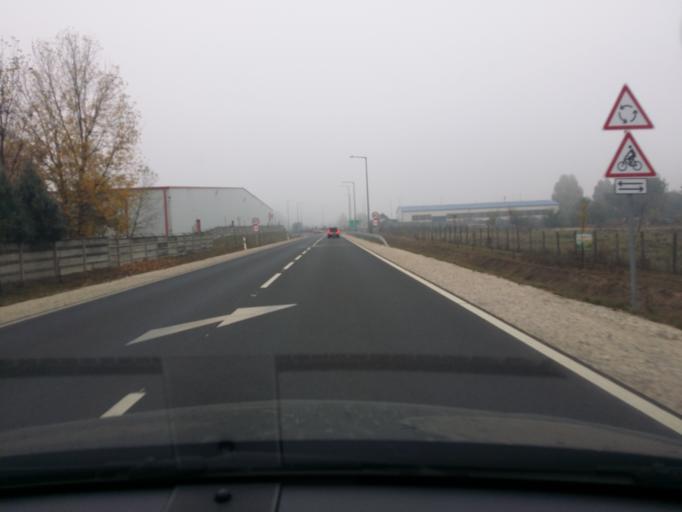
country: HU
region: Szabolcs-Szatmar-Bereg
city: Nyiregyhaza
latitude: 47.9550
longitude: 21.6555
